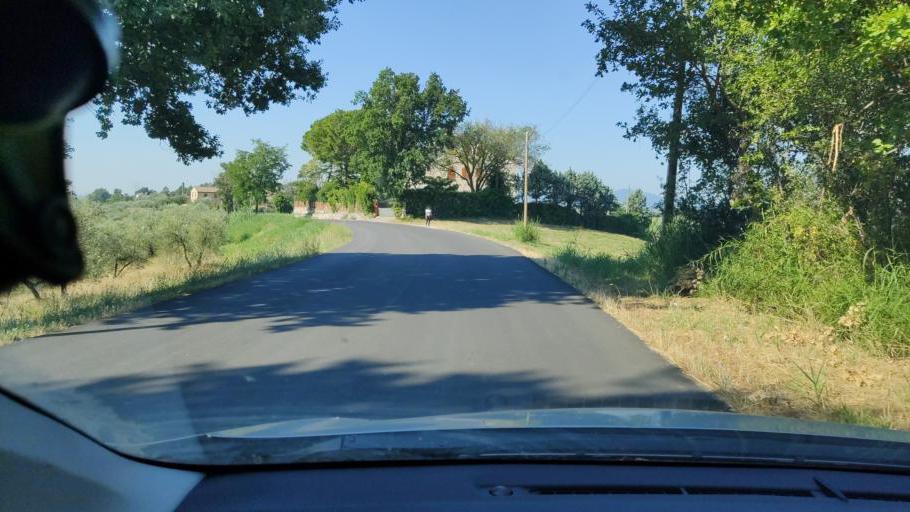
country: IT
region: Umbria
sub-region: Provincia di Terni
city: Fornole
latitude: 42.5352
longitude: 12.4516
